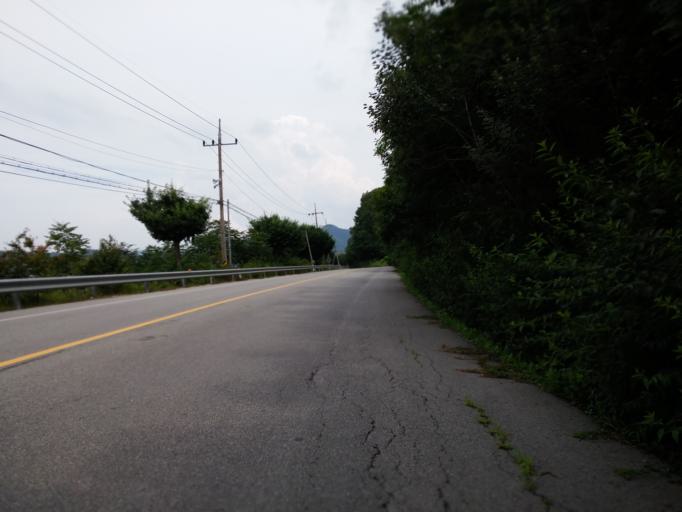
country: KR
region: Chungcheongnam-do
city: Gongju
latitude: 36.4439
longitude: 127.1877
